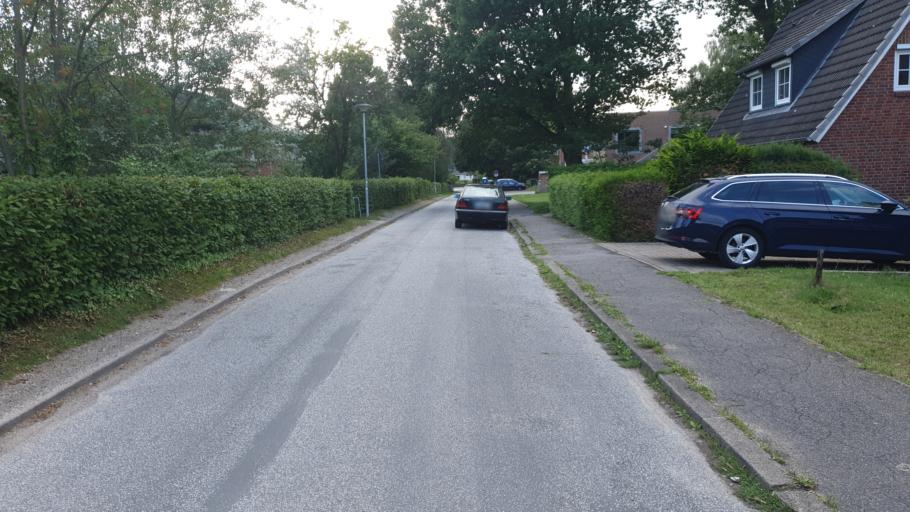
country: DE
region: Schleswig-Holstein
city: Luebeck
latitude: 53.8379
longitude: 10.7189
